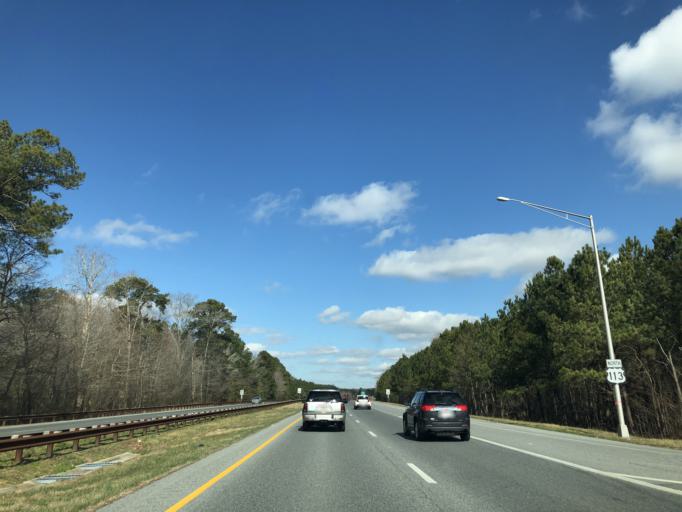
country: US
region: Maryland
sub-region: Worcester County
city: Berlin
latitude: 38.3579
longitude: -75.2137
